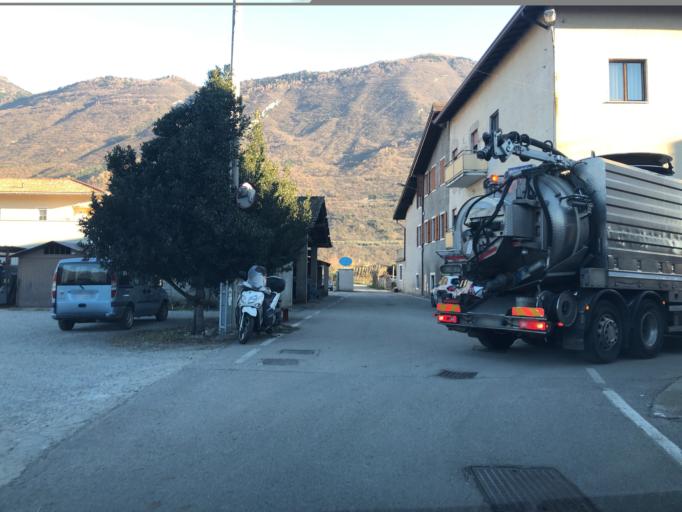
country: IT
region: Trentino-Alto Adige
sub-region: Provincia di Trento
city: Arco
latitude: 45.9044
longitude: 10.8888
